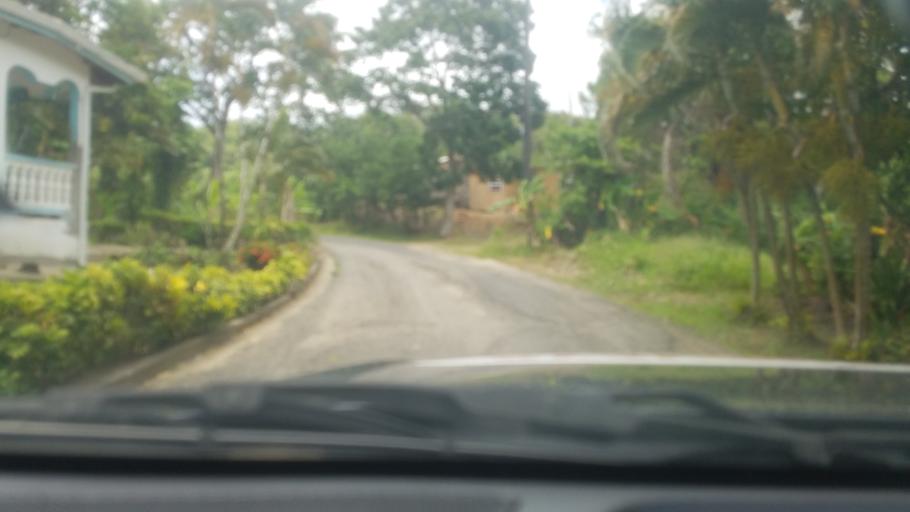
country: LC
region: Micoud Quarter
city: Micoud
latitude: 13.7994
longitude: -60.9482
